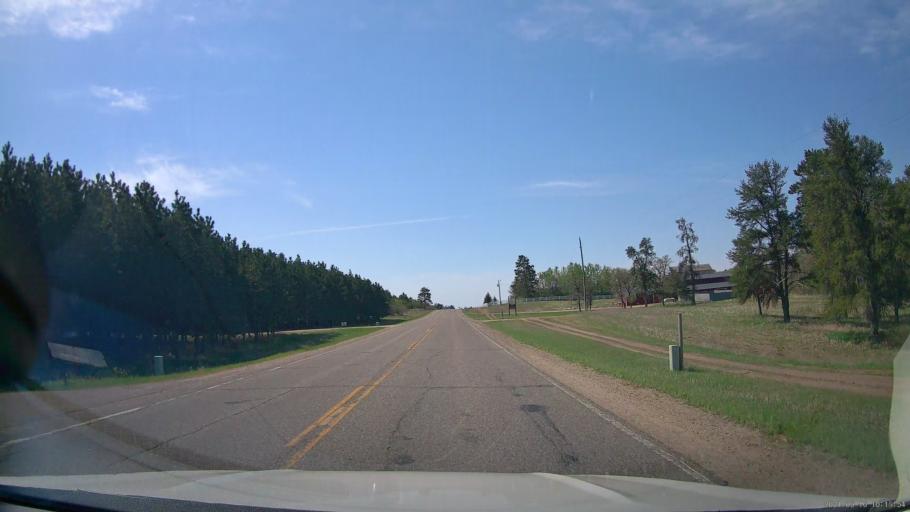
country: US
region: Minnesota
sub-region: Hubbard County
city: Park Rapids
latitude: 46.9728
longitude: -94.9527
